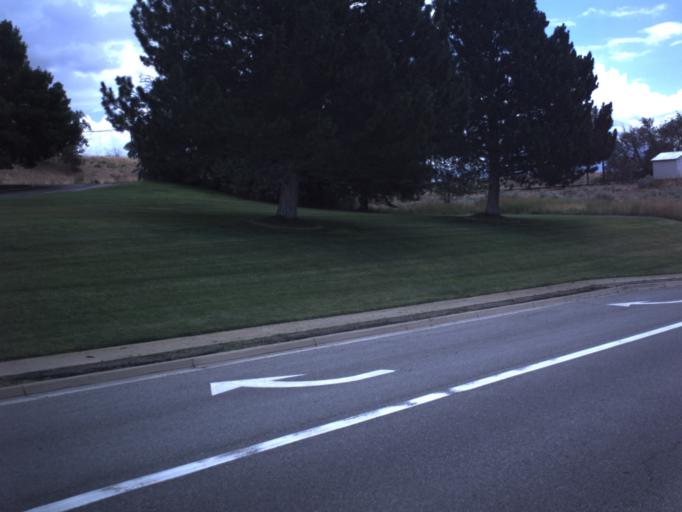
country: US
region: Utah
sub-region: Salt Lake County
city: Herriman
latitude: 40.5661
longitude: -112.0901
